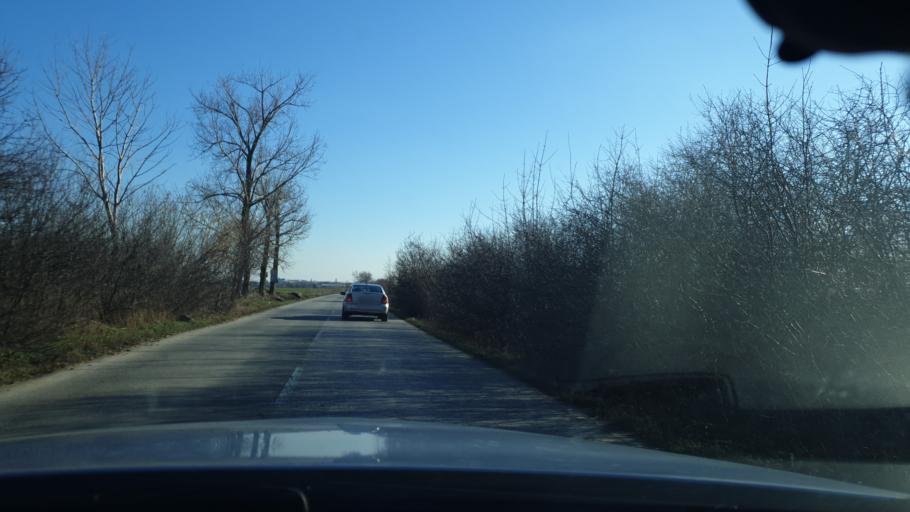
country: RS
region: Autonomna Pokrajina Vojvodina
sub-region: Sremski Okrug
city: Ruma
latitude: 45.0347
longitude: 19.8086
